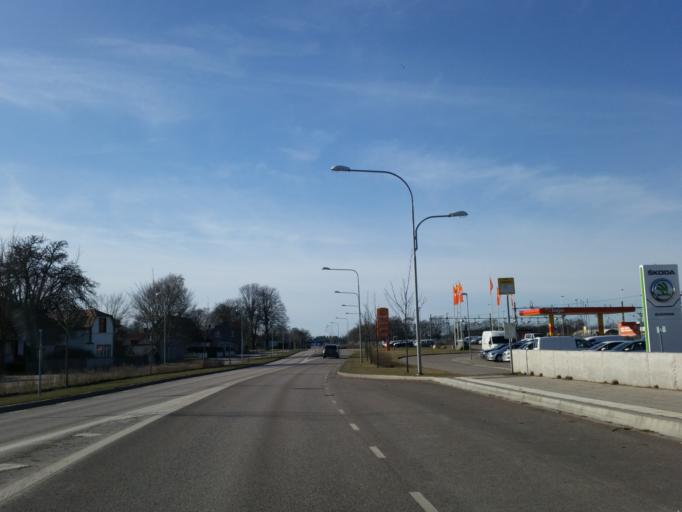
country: SE
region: Kalmar
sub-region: Kalmar Kommun
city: Kalmar
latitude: 56.6662
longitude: 16.3283
